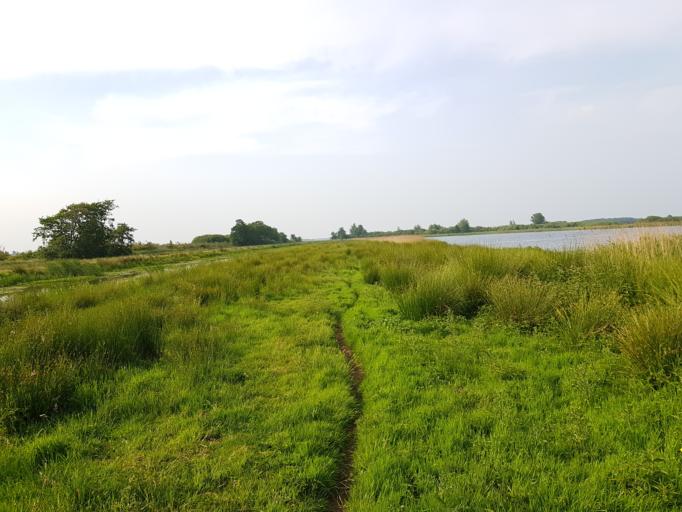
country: NL
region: Friesland
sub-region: Gemeente Opsterland
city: Gorredijk
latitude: 53.0339
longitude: 6.0453
